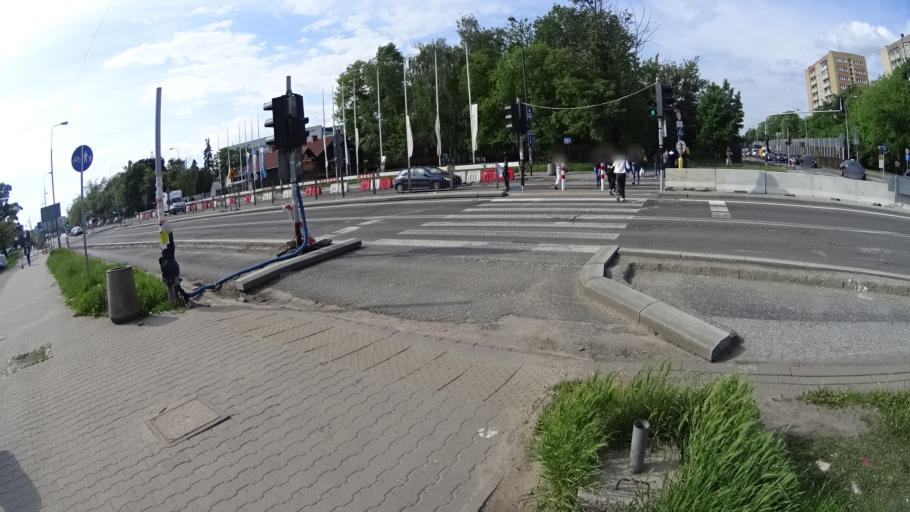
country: PL
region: Masovian Voivodeship
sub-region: Warszawa
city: Bemowo
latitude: 52.2408
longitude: 20.9358
